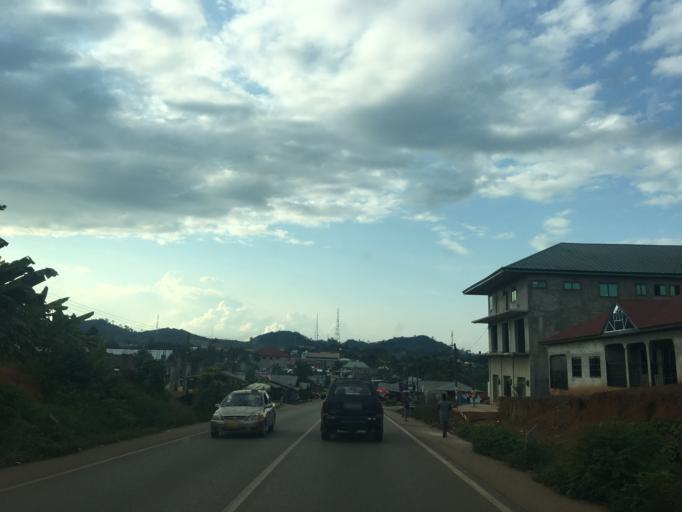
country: GH
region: Western
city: Bibiani
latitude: 6.4462
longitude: -2.3146
